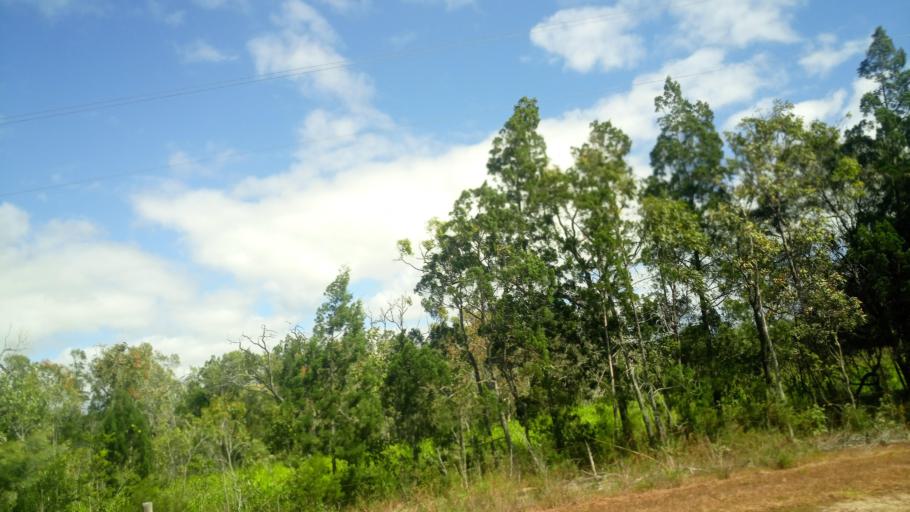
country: AU
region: Queensland
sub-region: Tablelands
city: Mareeba
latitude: -16.9654
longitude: 145.4465
